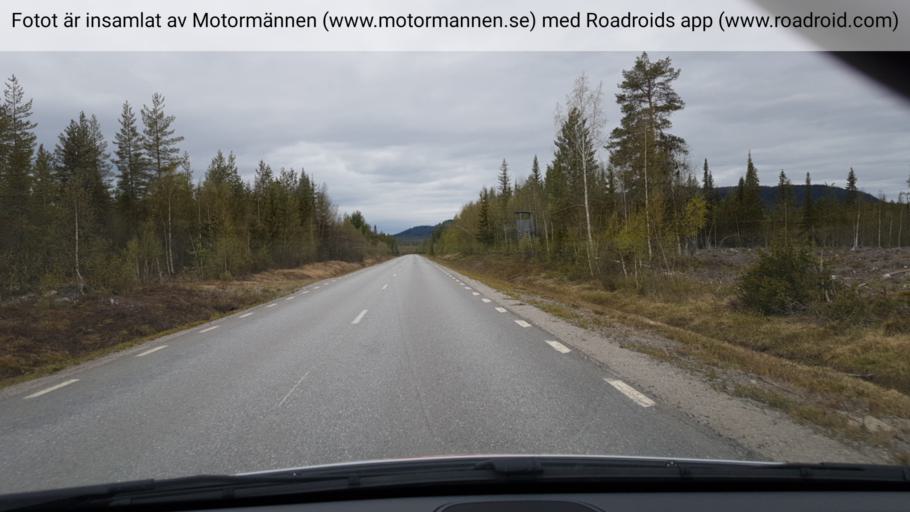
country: SE
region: Vaesterbotten
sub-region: Sorsele Kommun
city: Sorsele
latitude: 65.5147
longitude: 17.3593
